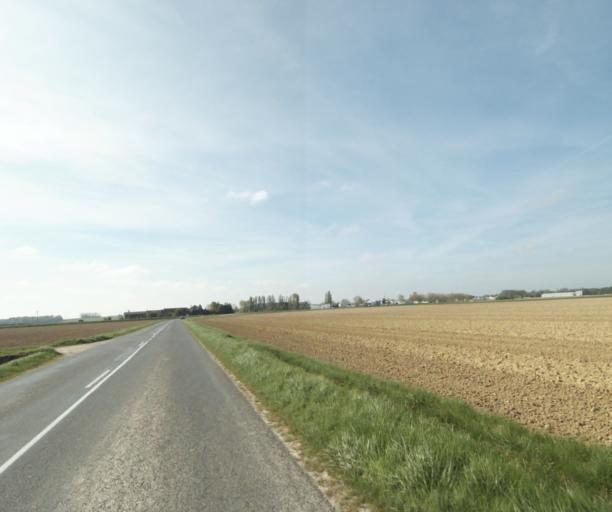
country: FR
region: Ile-de-France
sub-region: Departement de Seine-et-Marne
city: Nangis
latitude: 48.5667
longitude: 3.0391
